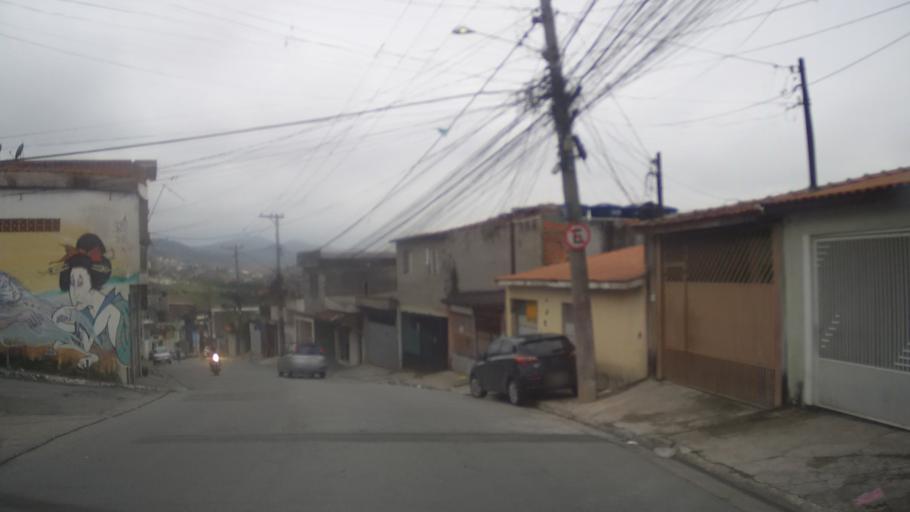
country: BR
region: Sao Paulo
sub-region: Guarulhos
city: Guarulhos
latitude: -23.4283
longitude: -46.5139
